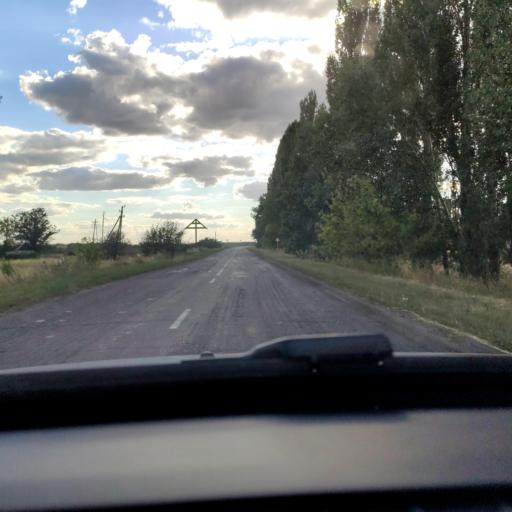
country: RU
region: Voronezj
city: Orlovo
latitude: 51.6155
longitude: 39.7977
